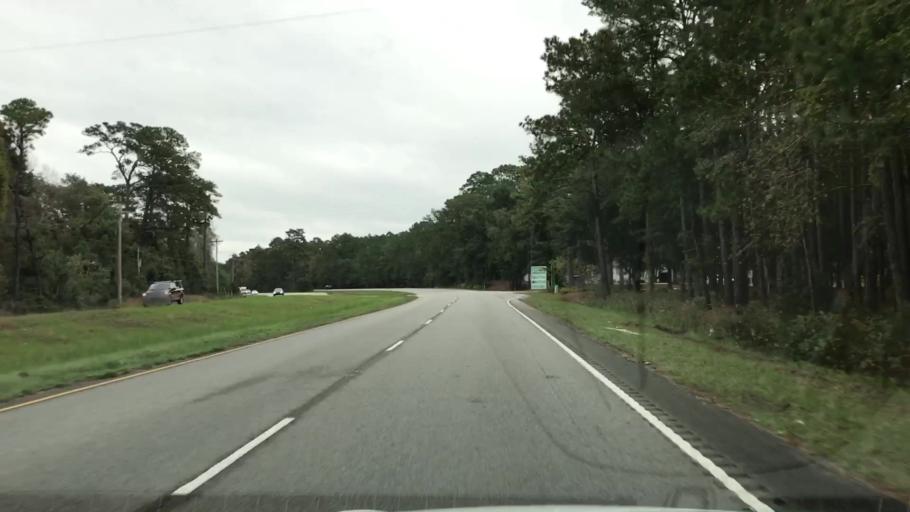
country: US
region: South Carolina
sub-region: Georgetown County
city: Georgetown
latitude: 33.3644
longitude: -79.2281
